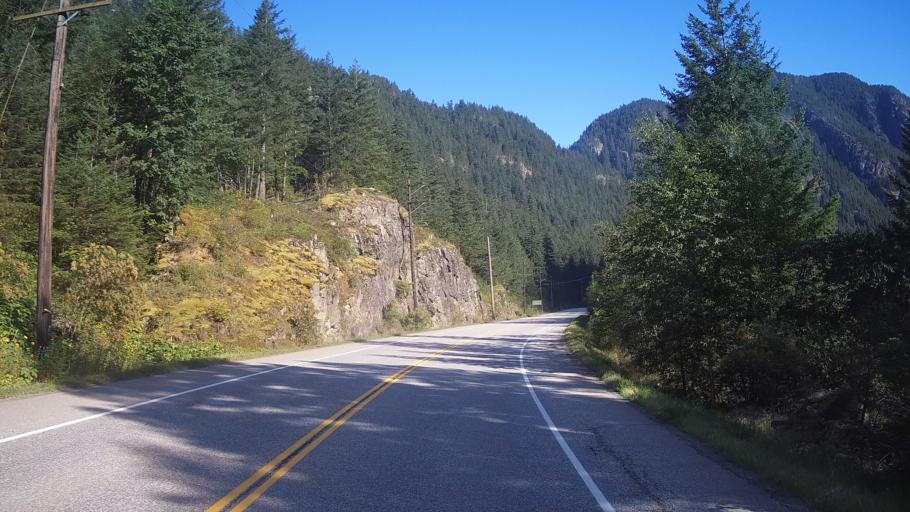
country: CA
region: British Columbia
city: Hope
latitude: 49.5973
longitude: -121.4139
